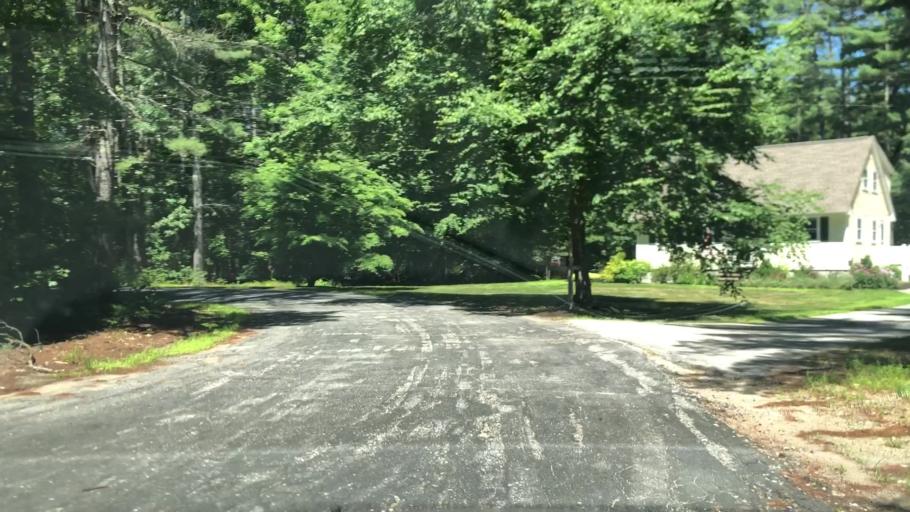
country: US
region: New Hampshire
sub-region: Hillsborough County
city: Milford
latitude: 42.8382
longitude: -71.5742
